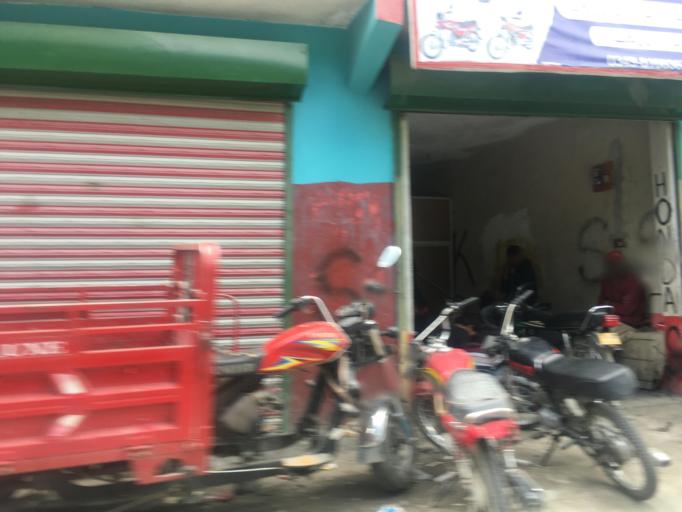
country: PK
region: Gilgit-Baltistan
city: Skardu
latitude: 35.2919
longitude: 75.6144
